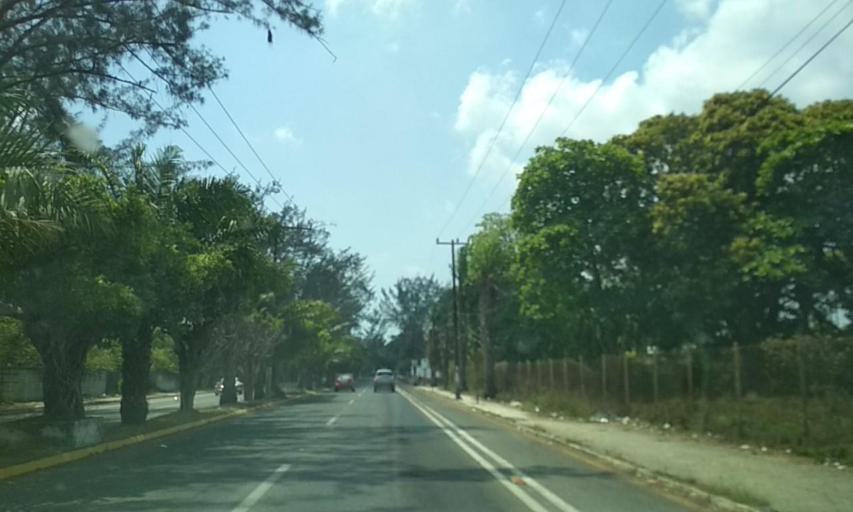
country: MX
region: Veracruz
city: Las Choapas
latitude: 17.9272
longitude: -94.0950
